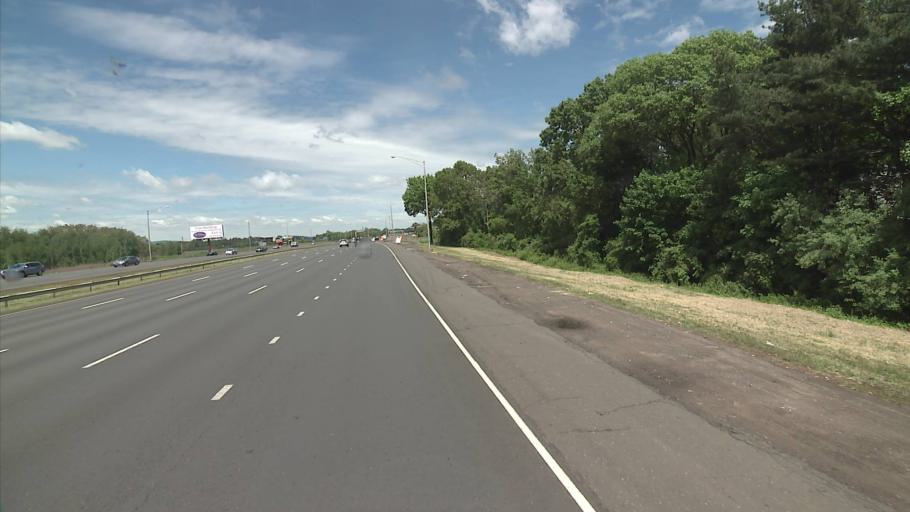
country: US
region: Connecticut
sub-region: New Haven County
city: New Haven
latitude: 41.3303
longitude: -72.8783
